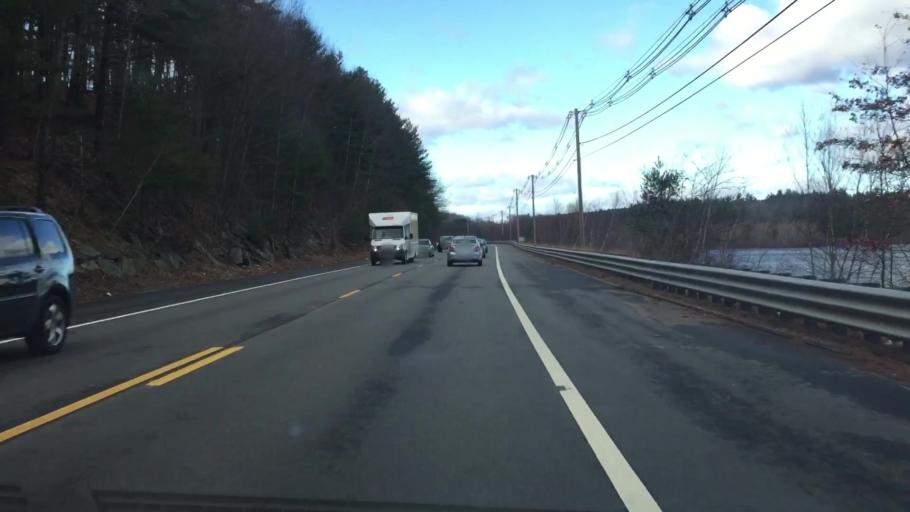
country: US
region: Massachusetts
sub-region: Worcester County
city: West Boylston
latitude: 42.3413
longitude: -71.7569
